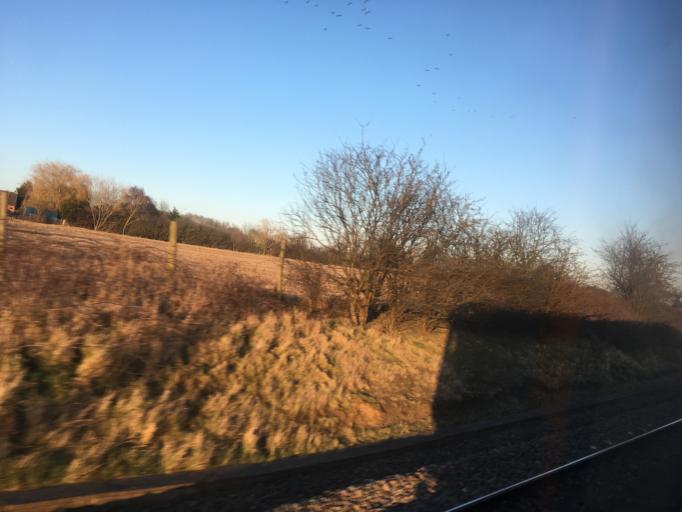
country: GB
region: England
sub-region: Derbyshire
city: Borrowash
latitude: 52.8993
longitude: -1.3628
